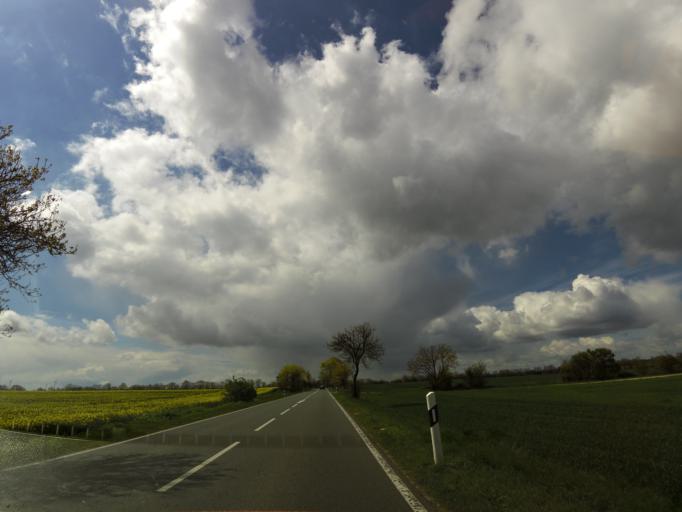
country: DE
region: Saxony-Anhalt
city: Hohendodeleben
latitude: 52.0799
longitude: 11.5226
